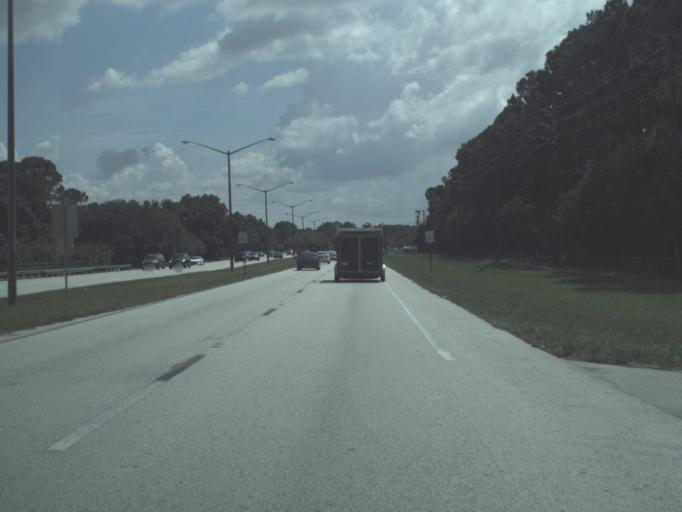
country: US
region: Florida
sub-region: Pinellas County
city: East Lake
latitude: 28.0881
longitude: -82.6994
